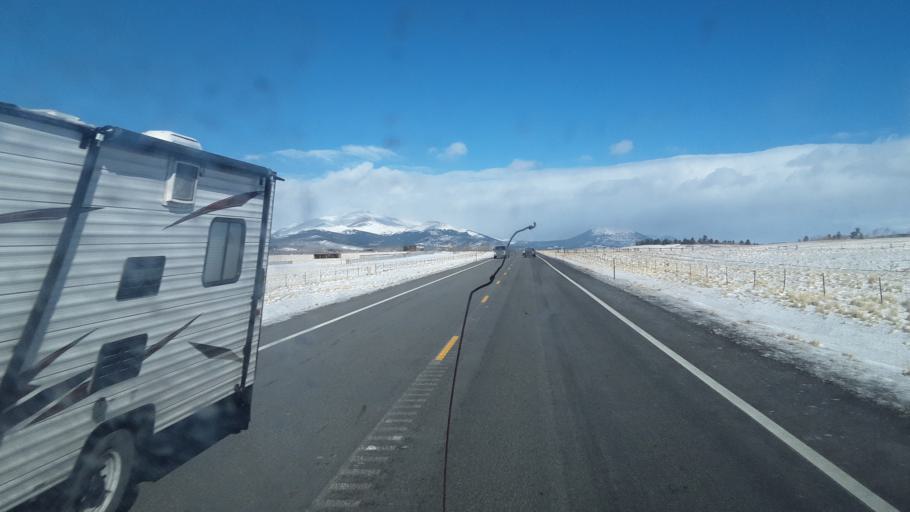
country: US
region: Colorado
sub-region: Park County
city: Fairplay
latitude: 39.1924
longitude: -105.9968
